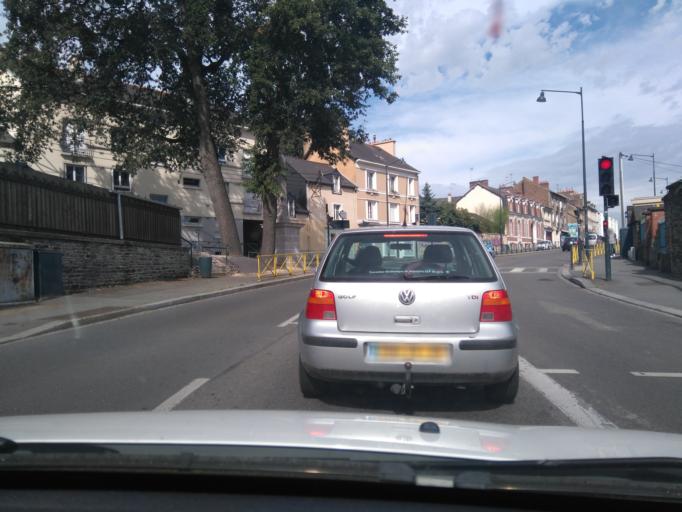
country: FR
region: Brittany
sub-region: Departement d'Ille-et-Vilaine
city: Rennes
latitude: 48.1020
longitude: -1.6582
